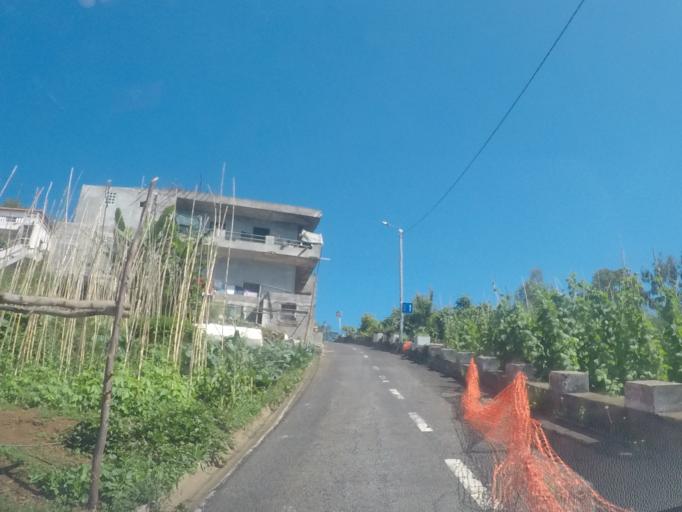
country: PT
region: Madeira
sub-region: Camara de Lobos
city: Curral das Freiras
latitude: 32.6827
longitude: -16.9684
